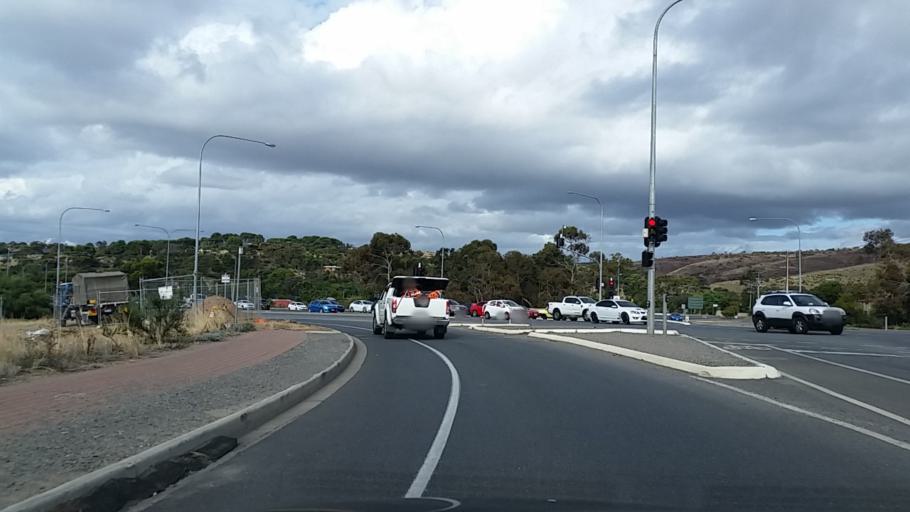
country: AU
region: South Australia
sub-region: Onkaparinga
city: Noarlunga
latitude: -35.1799
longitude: 138.4955
